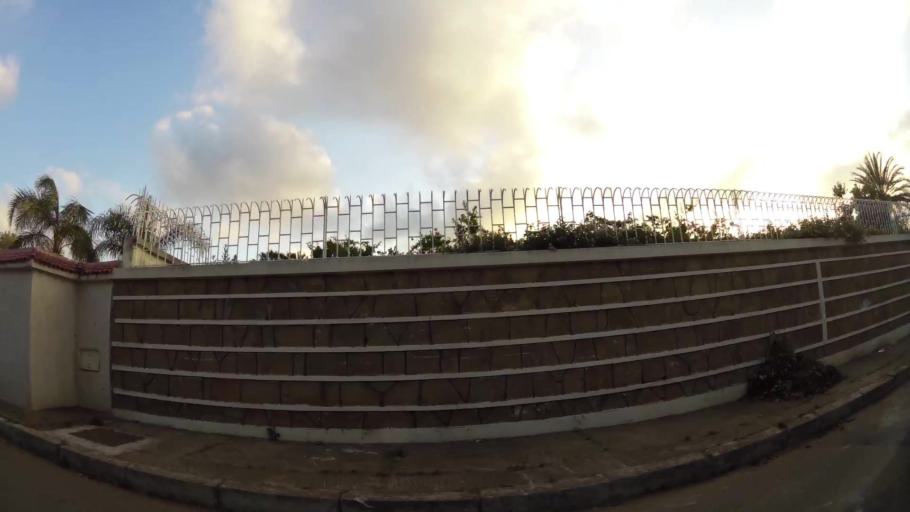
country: MA
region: Rabat-Sale-Zemmour-Zaer
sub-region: Rabat
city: Rabat
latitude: 33.9739
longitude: -6.8370
